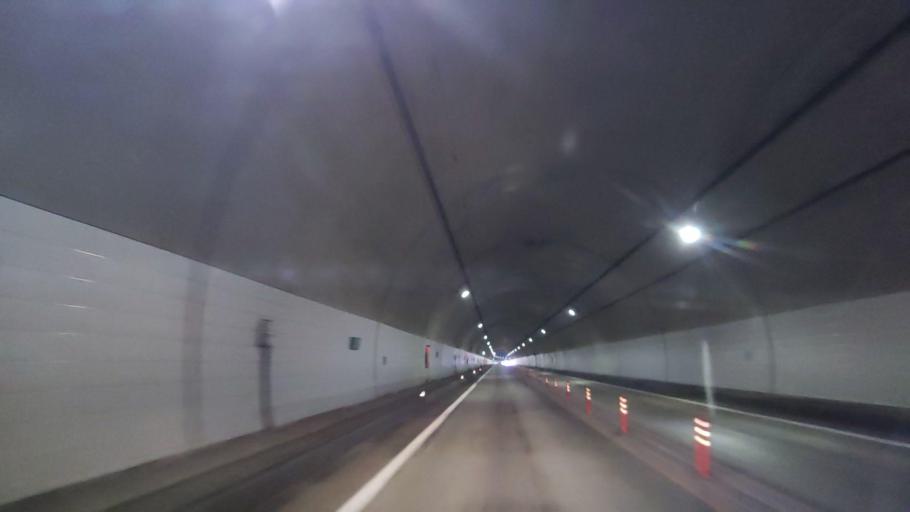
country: JP
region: Akita
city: Odate
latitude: 40.3651
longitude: 140.6974
